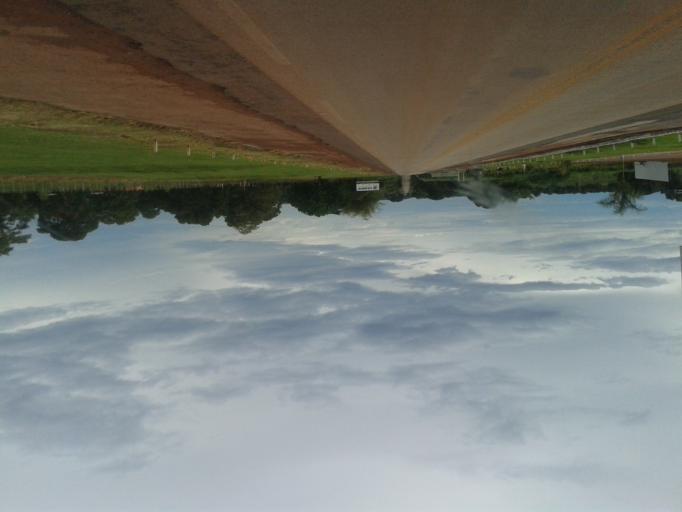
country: BR
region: Goias
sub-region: Mozarlandia
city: Mozarlandia
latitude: -14.7556
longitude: -50.5402
